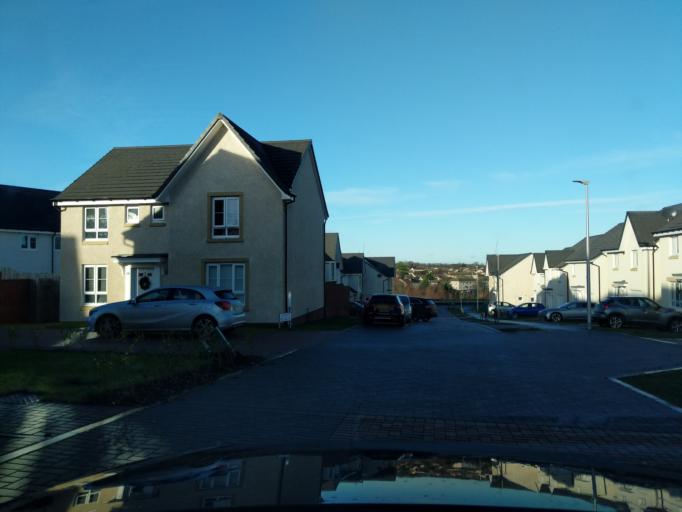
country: GB
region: Scotland
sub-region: Midlothian
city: Loanhead
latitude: 55.8945
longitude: -3.1526
